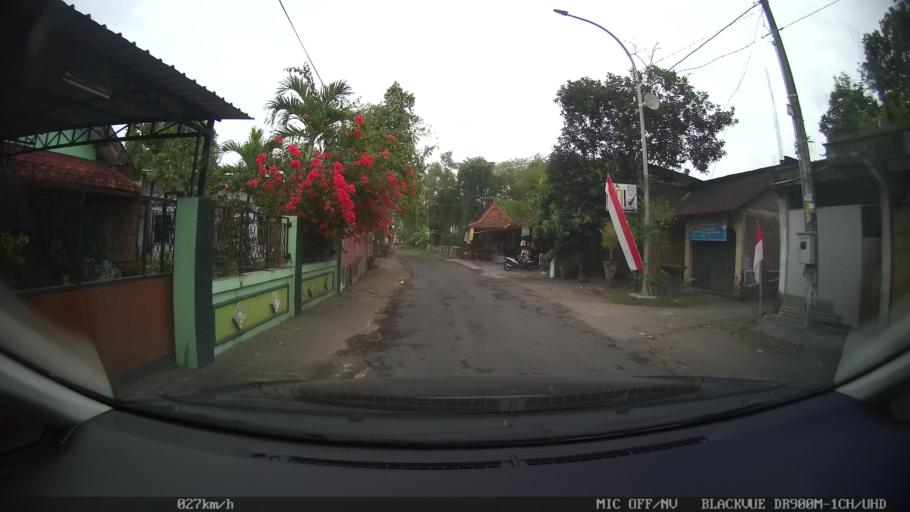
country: ID
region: Daerah Istimewa Yogyakarta
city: Sewon
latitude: -7.8583
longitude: 110.3990
